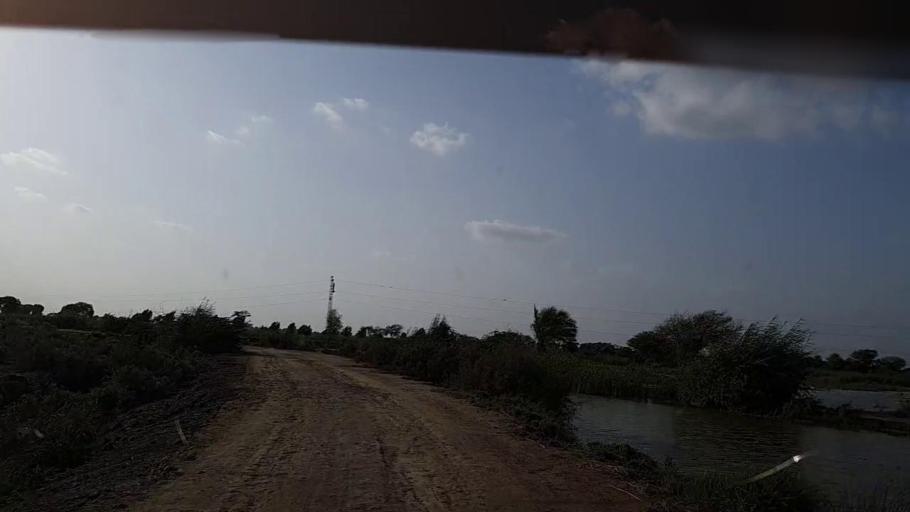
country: PK
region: Sindh
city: Badin
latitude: 24.5595
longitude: 68.8973
